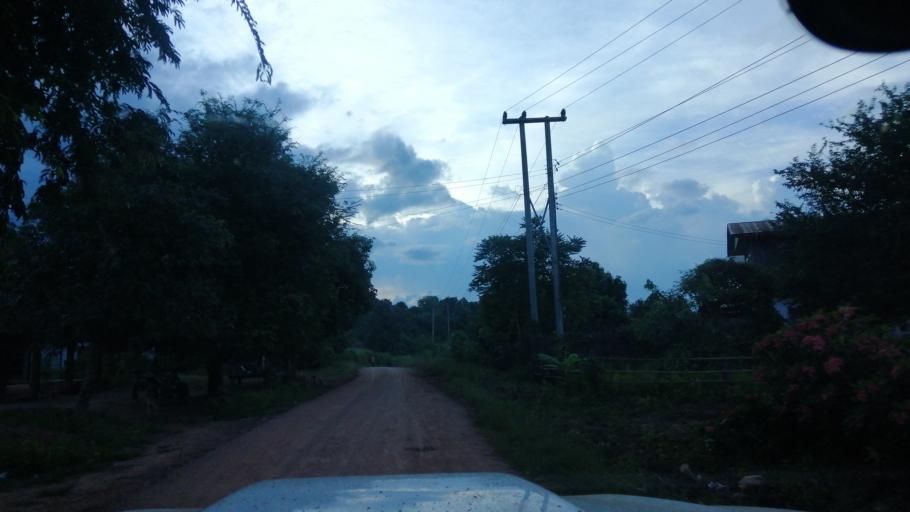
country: TH
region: Uttaradit
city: Ban Khok
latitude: 17.8693
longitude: 101.0890
